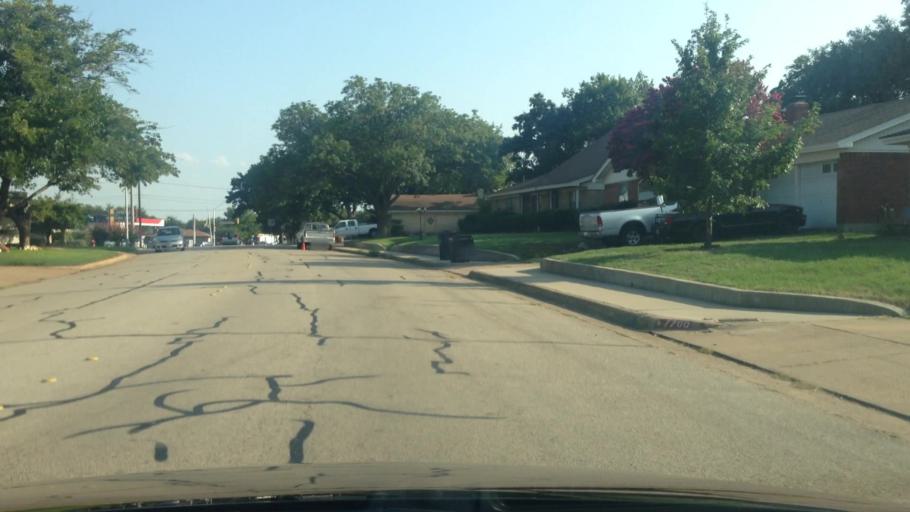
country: US
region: Texas
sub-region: Tarrant County
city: Edgecliff Village
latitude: 32.6372
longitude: -97.3400
